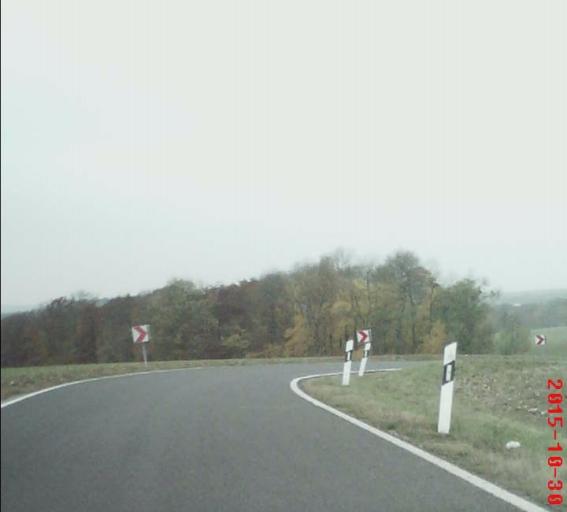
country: DE
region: Thuringia
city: Heuthen
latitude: 51.3099
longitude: 10.2110
